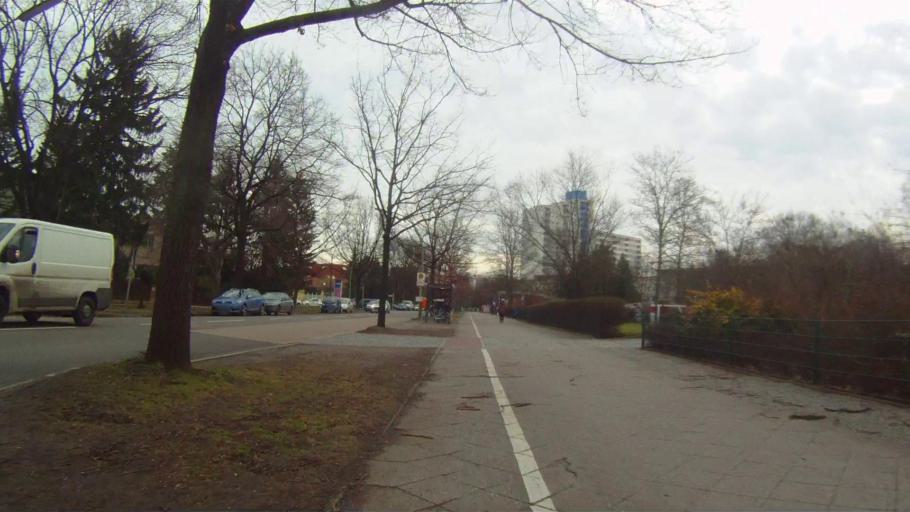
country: DE
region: Berlin
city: Lichtenrade
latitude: 52.3957
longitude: 13.3984
